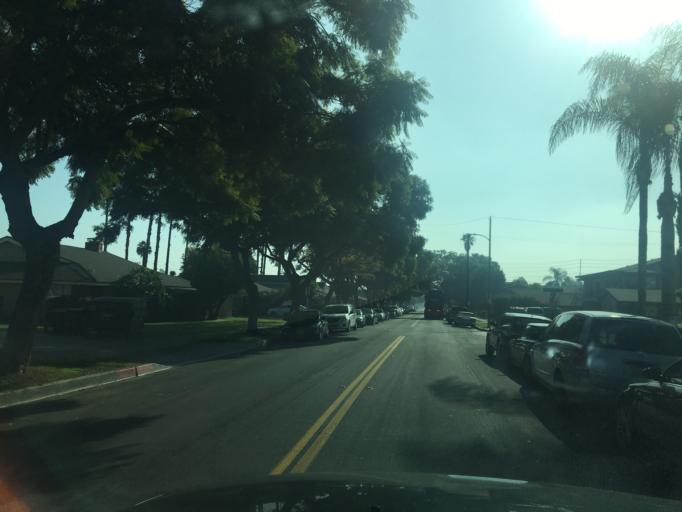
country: US
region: California
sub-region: Orange County
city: Tustin
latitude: 33.7361
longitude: -117.8318
